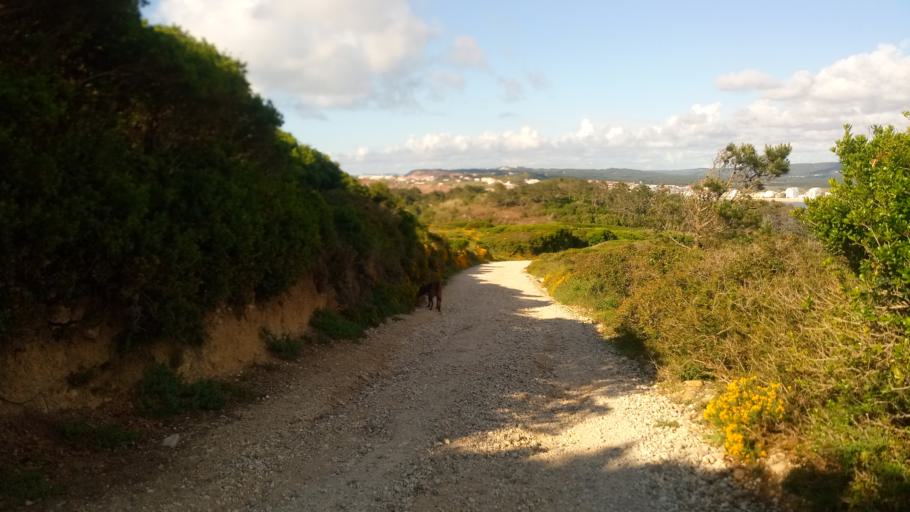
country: PT
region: Leiria
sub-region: Caldas da Rainha
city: Caldas da Rainha
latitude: 39.5007
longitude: -9.1569
